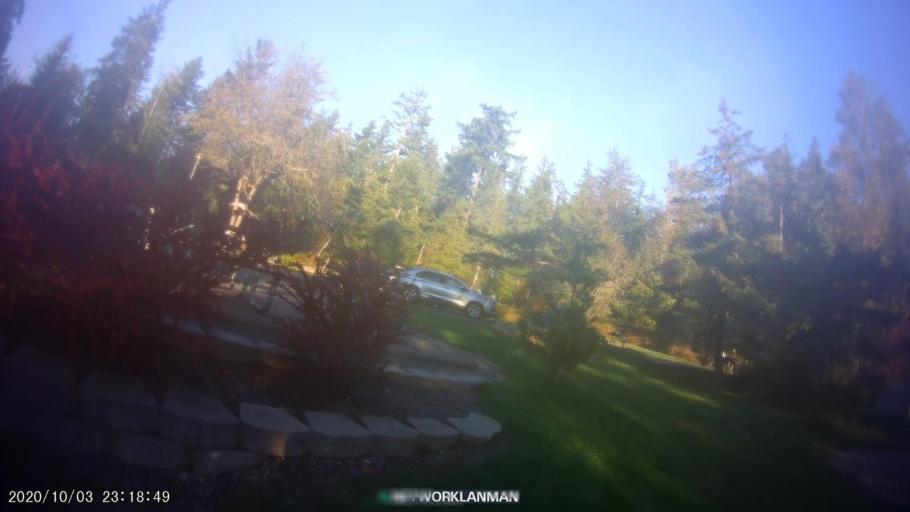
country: US
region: Washington
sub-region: Pierce County
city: Eatonville
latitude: 46.8020
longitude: -122.3028
